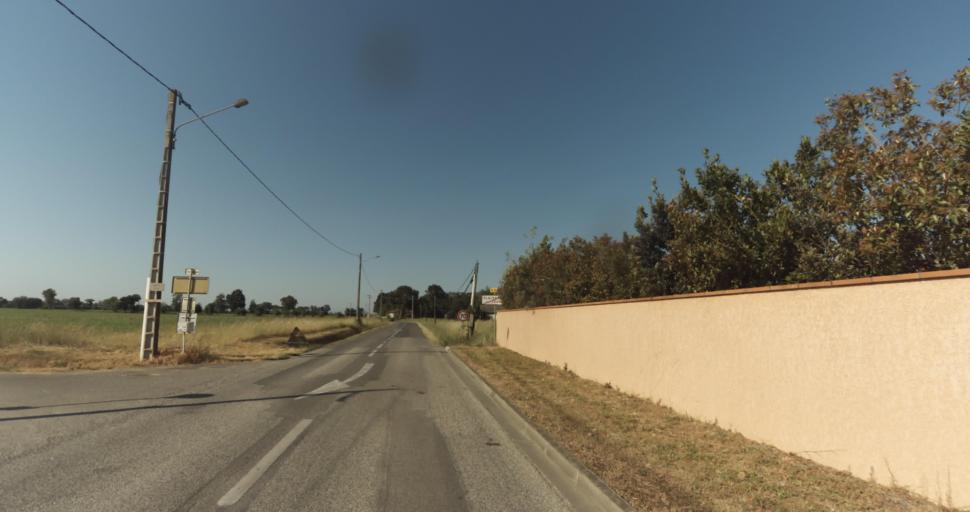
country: FR
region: Midi-Pyrenees
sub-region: Departement de la Haute-Garonne
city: Plaisance-du-Touch
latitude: 43.5529
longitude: 1.2947
